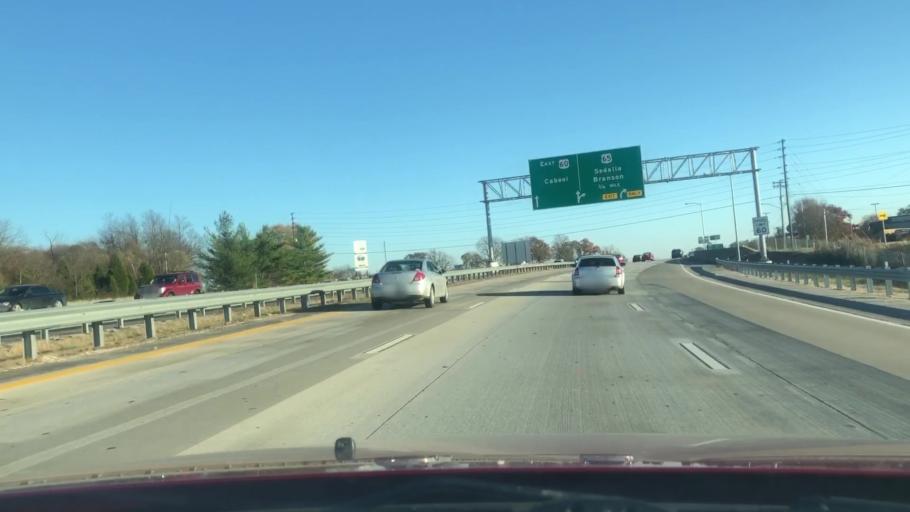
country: US
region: Missouri
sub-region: Greene County
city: Springfield
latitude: 37.1374
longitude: -93.2491
